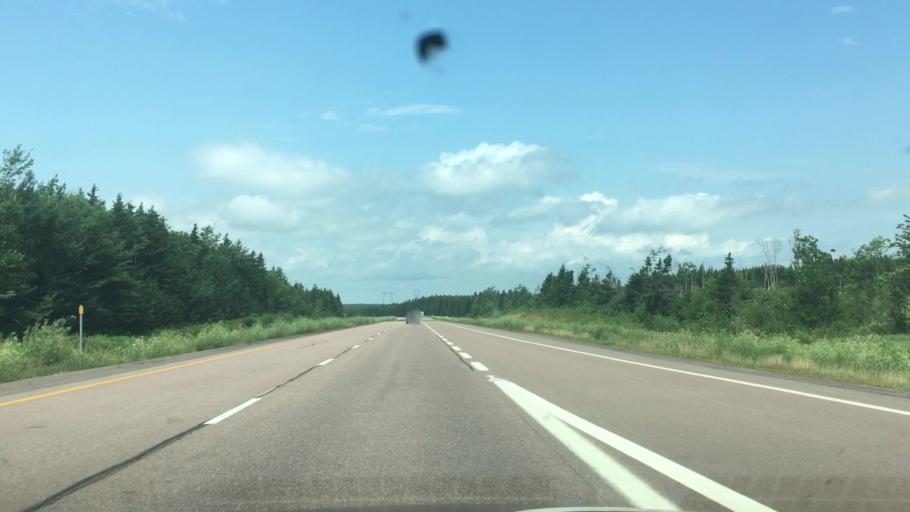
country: CA
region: New Brunswick
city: Sackville
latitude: 45.9622
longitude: -64.4190
